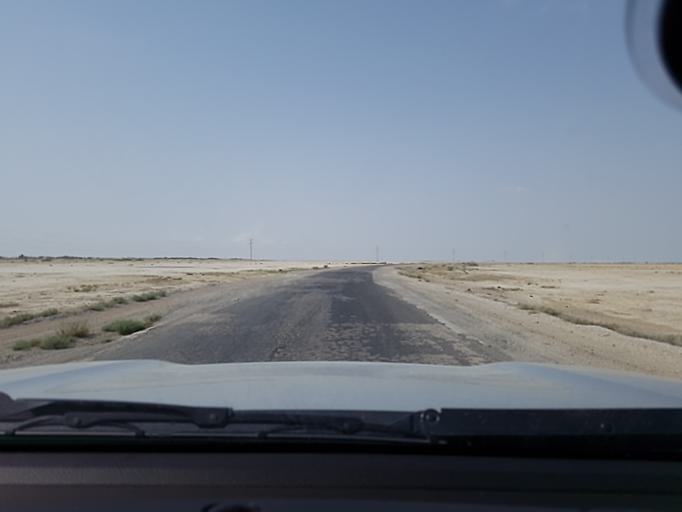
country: TM
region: Balkan
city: Gumdag
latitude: 38.7666
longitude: 54.5850
